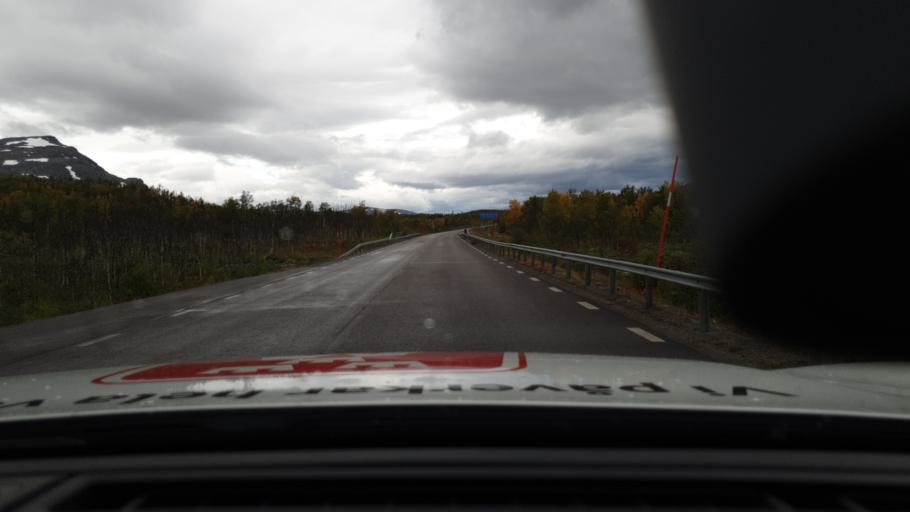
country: NO
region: Troms
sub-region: Bardu
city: Setermoen
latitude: 68.4261
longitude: 18.3557
